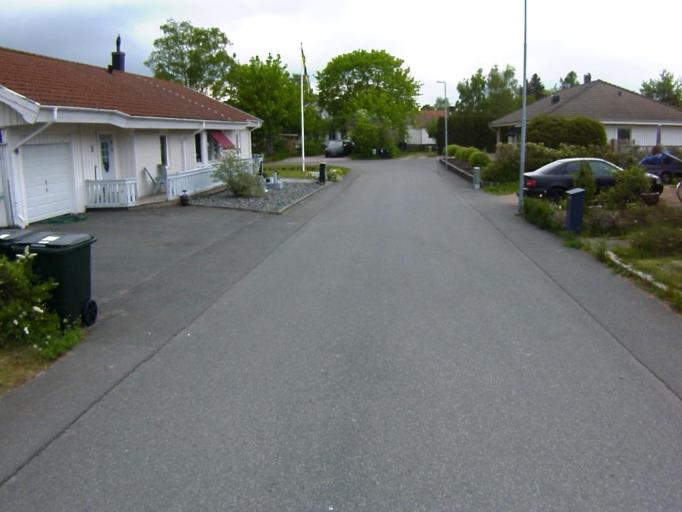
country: SE
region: Skane
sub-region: Kristianstads Kommun
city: Ahus
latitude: 55.9174
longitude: 14.2794
